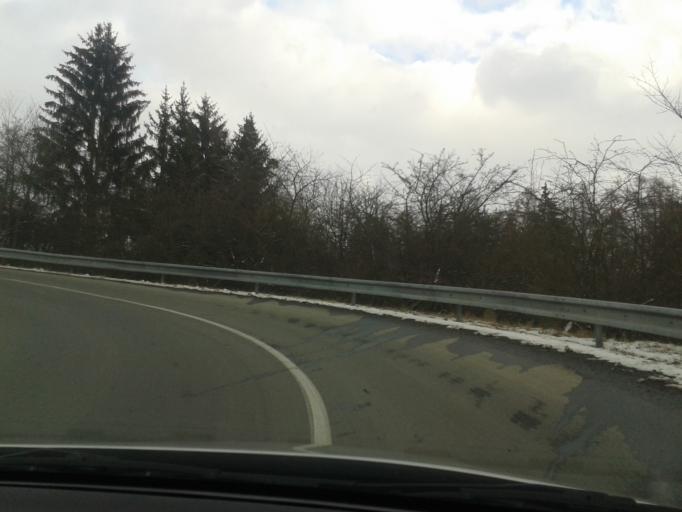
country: CZ
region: Olomoucky
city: Konice
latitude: 49.5938
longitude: 16.8914
